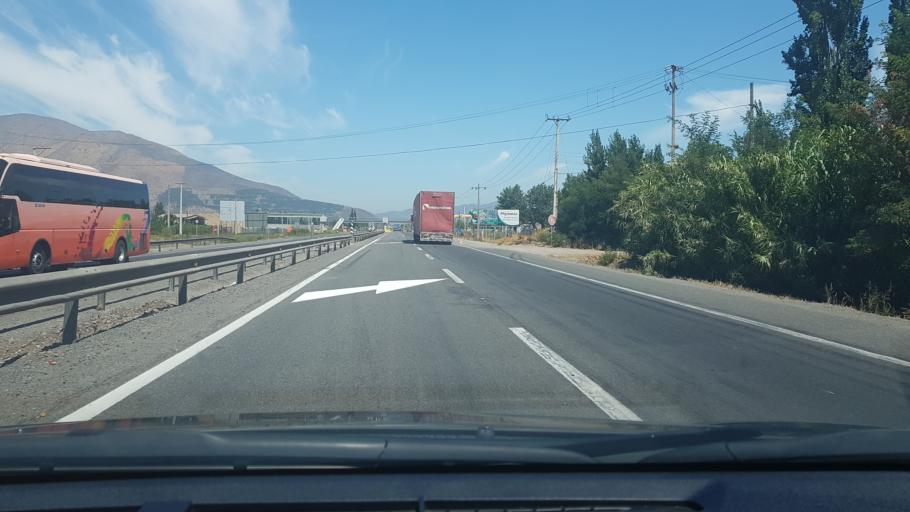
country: CL
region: Valparaiso
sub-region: Provincia de San Felipe
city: Llaillay
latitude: -32.8488
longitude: -70.9571
